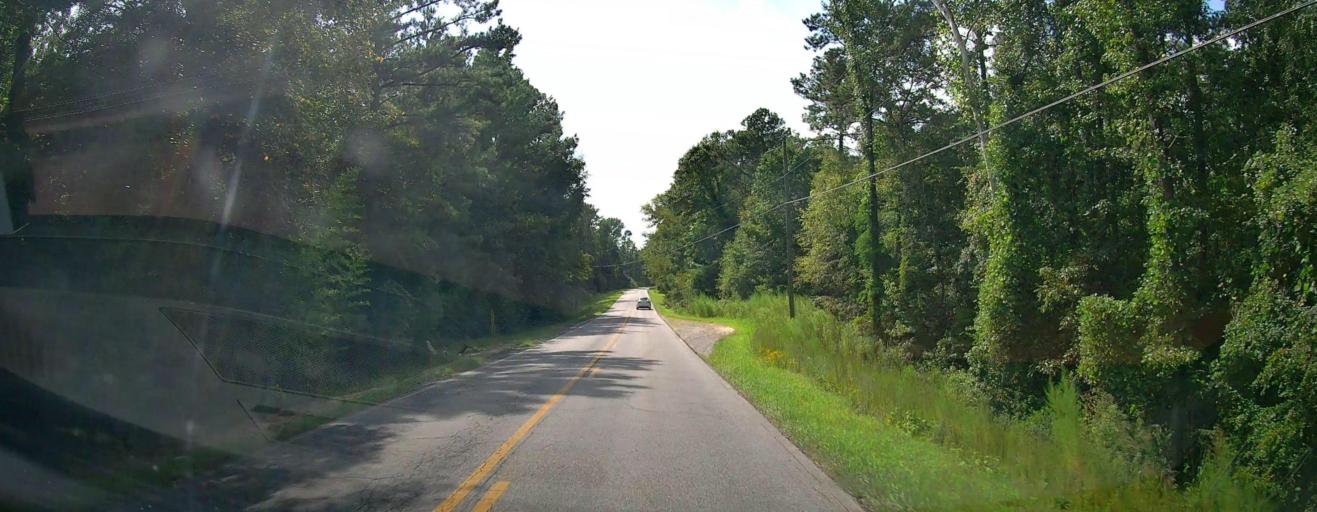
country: US
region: Alabama
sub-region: Russell County
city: Phenix City
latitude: 32.5905
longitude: -84.9319
